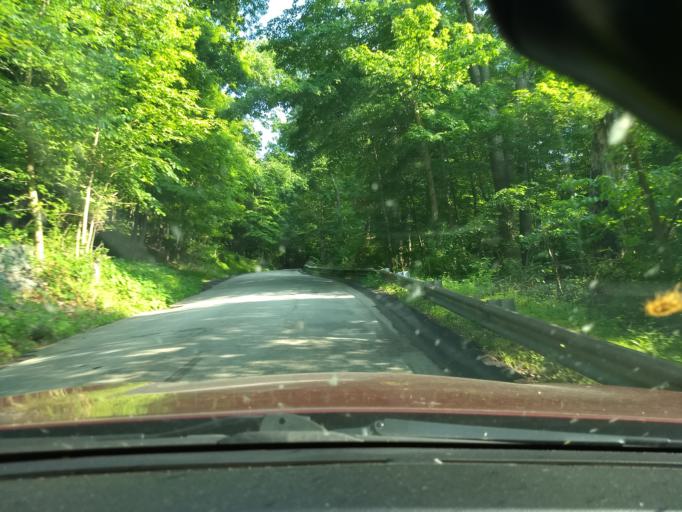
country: US
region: Pennsylvania
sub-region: Westmoreland County
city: Trafford
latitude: 40.3690
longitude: -79.7641
